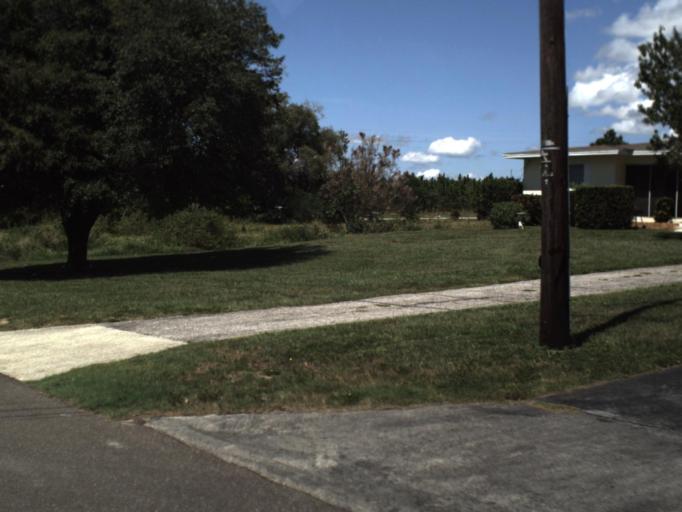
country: US
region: Florida
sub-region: Polk County
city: Crooked Lake Park
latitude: 27.8430
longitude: -81.5589
